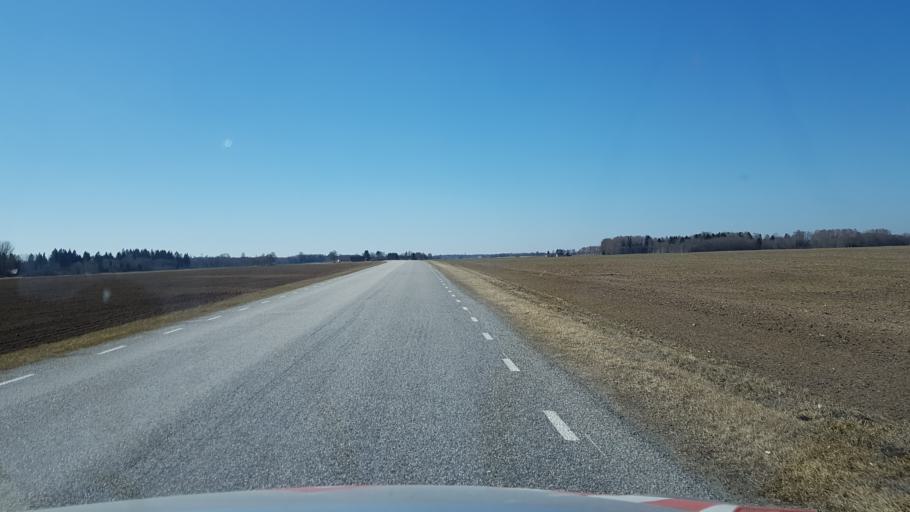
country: EE
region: Laeaene-Virumaa
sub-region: Vinni vald
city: Vinni
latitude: 59.0654
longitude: 26.4807
